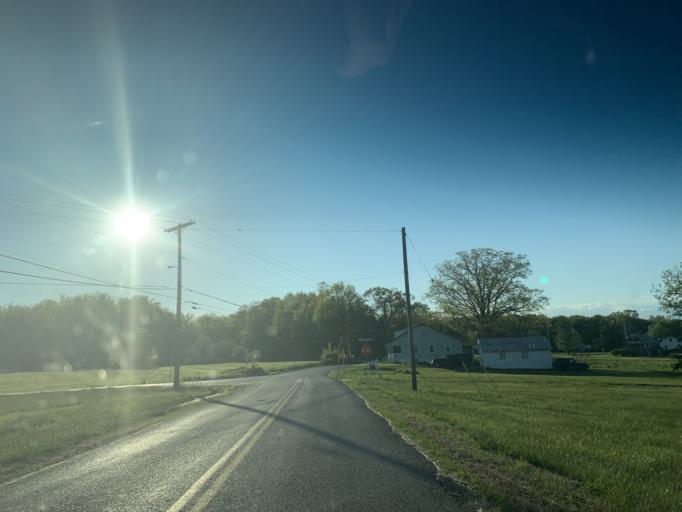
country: US
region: Maryland
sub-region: Harford County
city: Aberdeen
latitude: 39.5534
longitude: -76.1947
